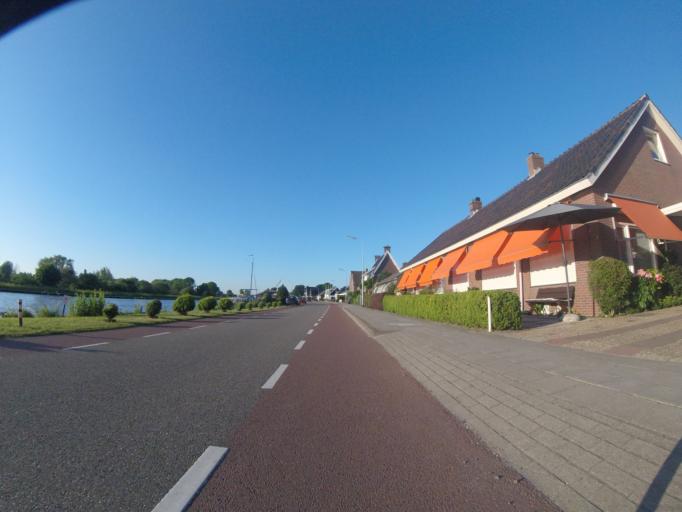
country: NL
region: North Holland
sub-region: Gemeente Haarlem
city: Haarlem
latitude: 52.3515
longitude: 4.6752
